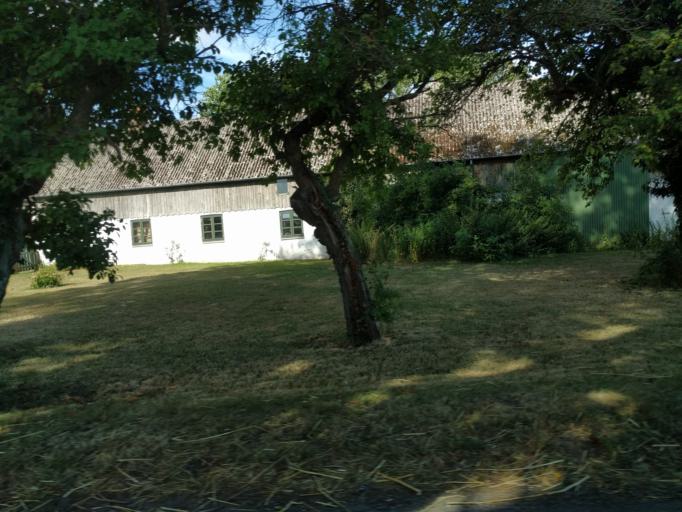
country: DK
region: Zealand
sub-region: Vordingborg Kommune
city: Stege
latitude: 54.9648
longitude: 12.2955
